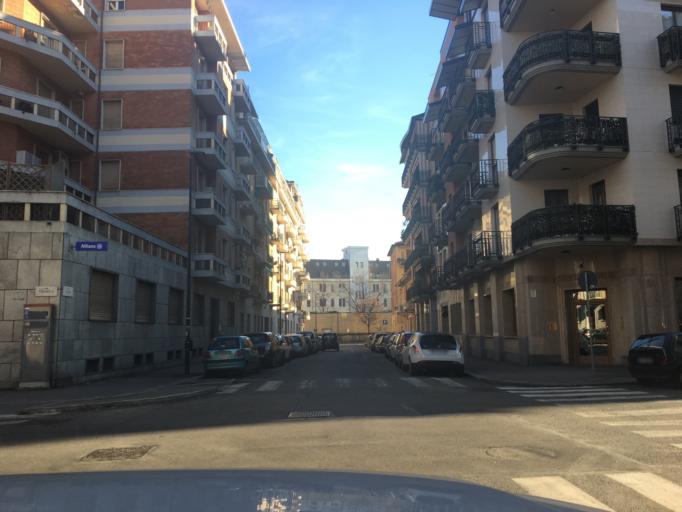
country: IT
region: Piedmont
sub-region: Provincia di Torino
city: Lesna
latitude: 45.0505
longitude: 7.6503
